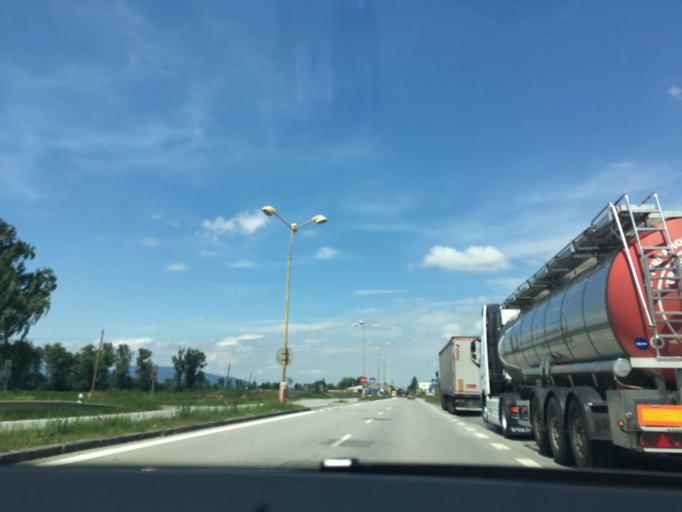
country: SK
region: Kosicky
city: Trebisov
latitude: 48.6560
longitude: 21.7131
